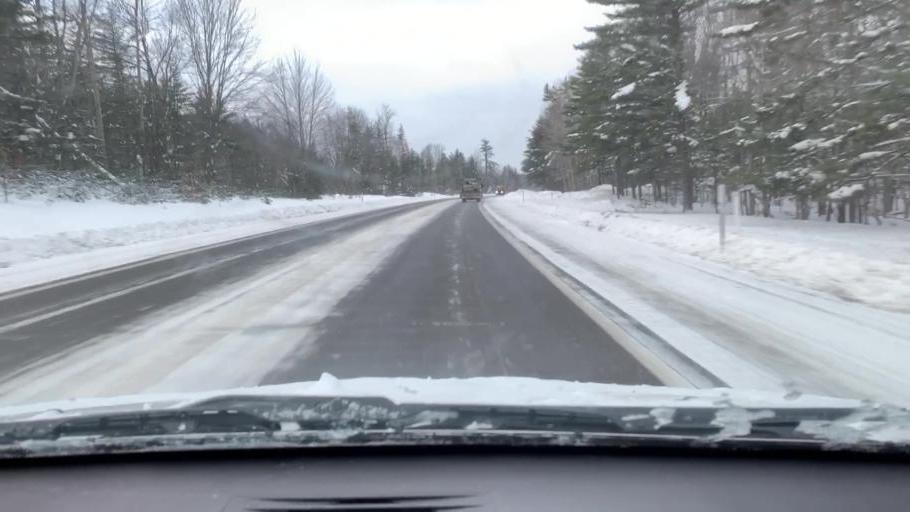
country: US
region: Michigan
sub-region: Kalkaska County
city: Kalkaska
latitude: 44.6486
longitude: -85.2715
